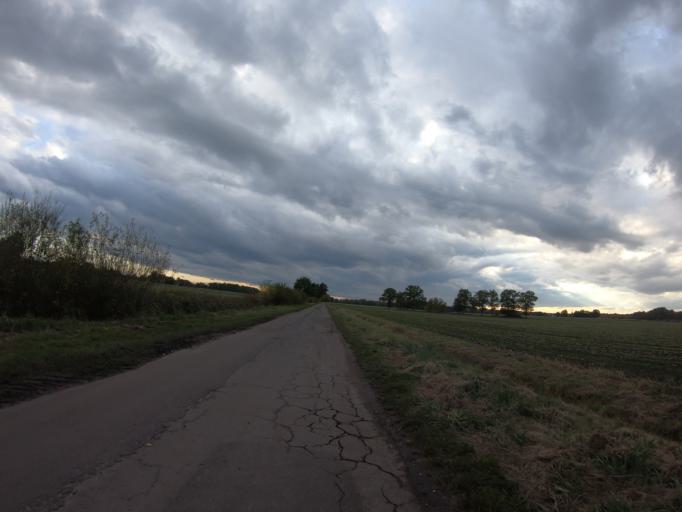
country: DE
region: Lower Saxony
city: Wagenhoff
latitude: 52.5396
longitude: 10.5462
